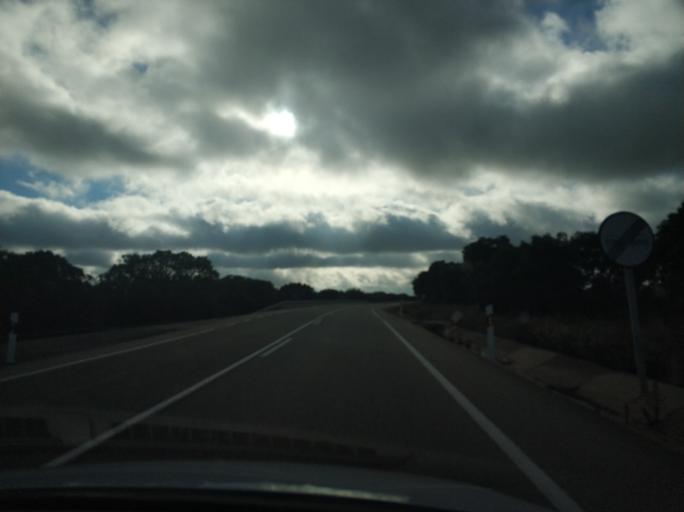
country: ES
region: Castille and Leon
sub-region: Provincia de Soria
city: Fuentecambron
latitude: 41.5005
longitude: -3.3061
